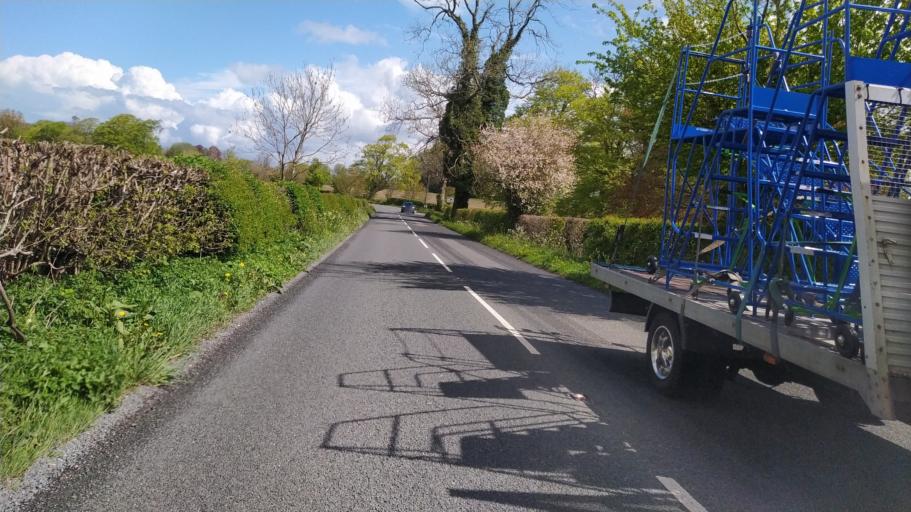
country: GB
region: England
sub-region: Wiltshire
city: Kilmington
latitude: 51.1409
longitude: -2.2824
